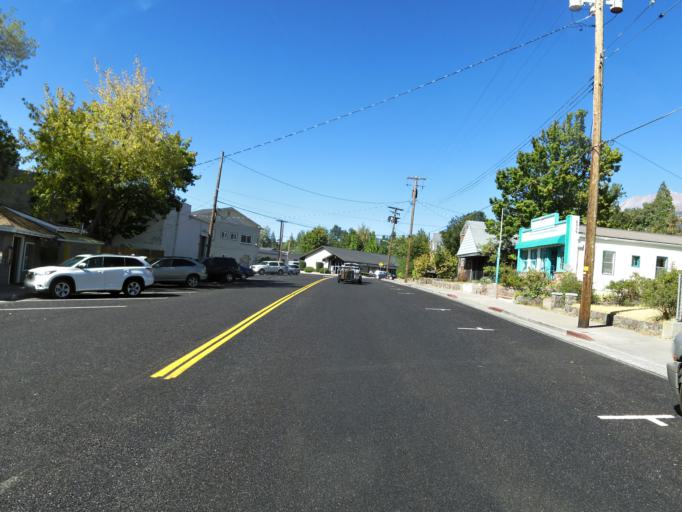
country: US
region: California
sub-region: Siskiyou County
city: Mount Shasta
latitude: 41.3125
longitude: -122.3110
